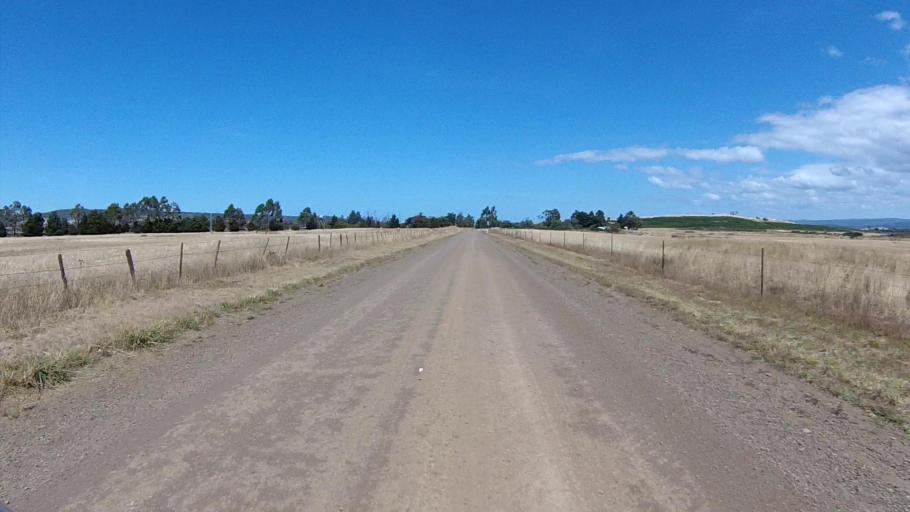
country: AU
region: Tasmania
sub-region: Break O'Day
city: St Helens
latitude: -41.9991
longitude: 148.0673
